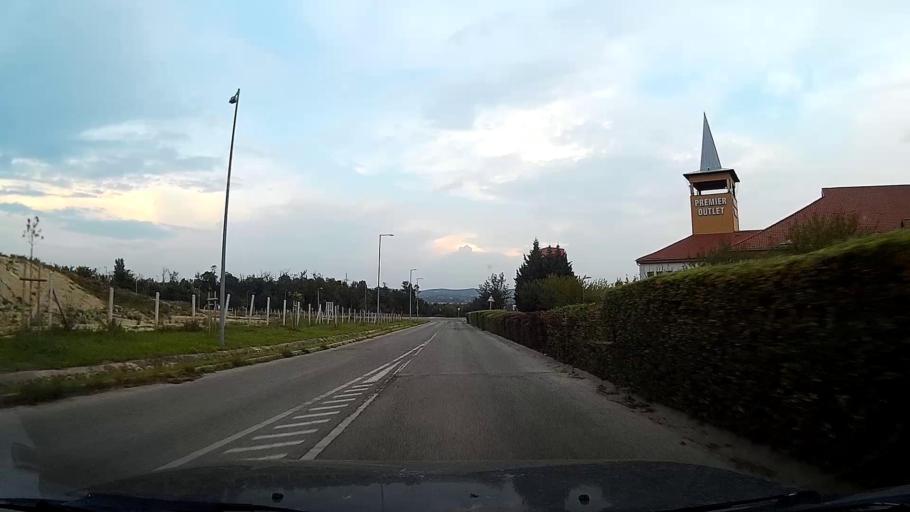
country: HU
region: Pest
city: Toeroekbalint
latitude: 47.4651
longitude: 18.8897
